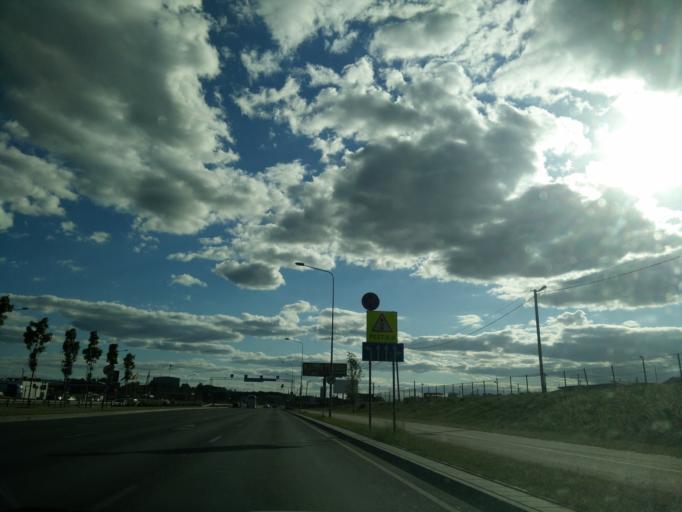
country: LT
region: Vilnius County
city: Lazdynai
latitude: 54.6601
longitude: 25.1628
